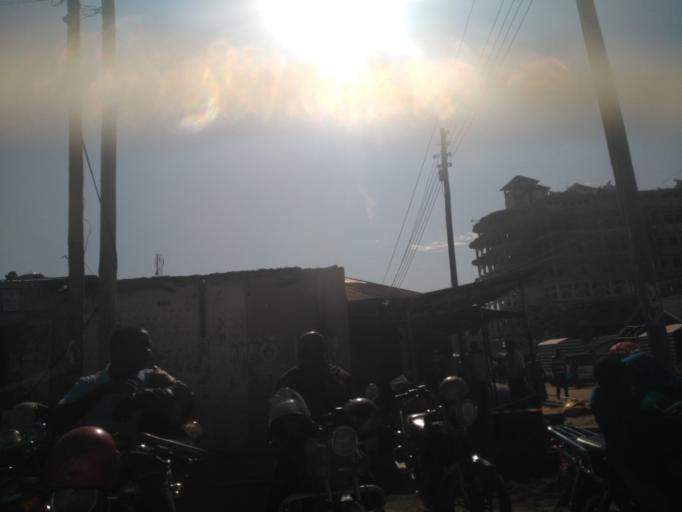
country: TZ
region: Mwanza
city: Mwanza
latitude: -2.5061
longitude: 32.8965
